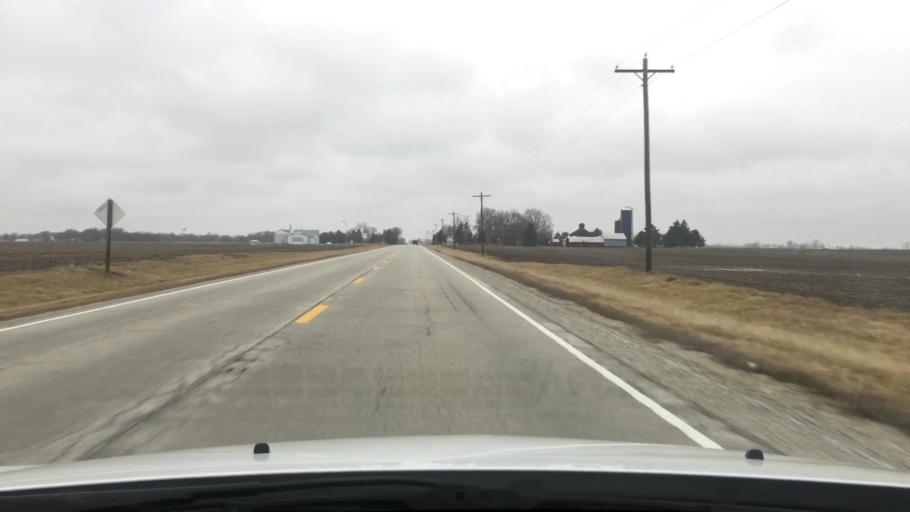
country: US
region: Illinois
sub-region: Iroquois County
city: Clifton
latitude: 40.8855
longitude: -87.9254
